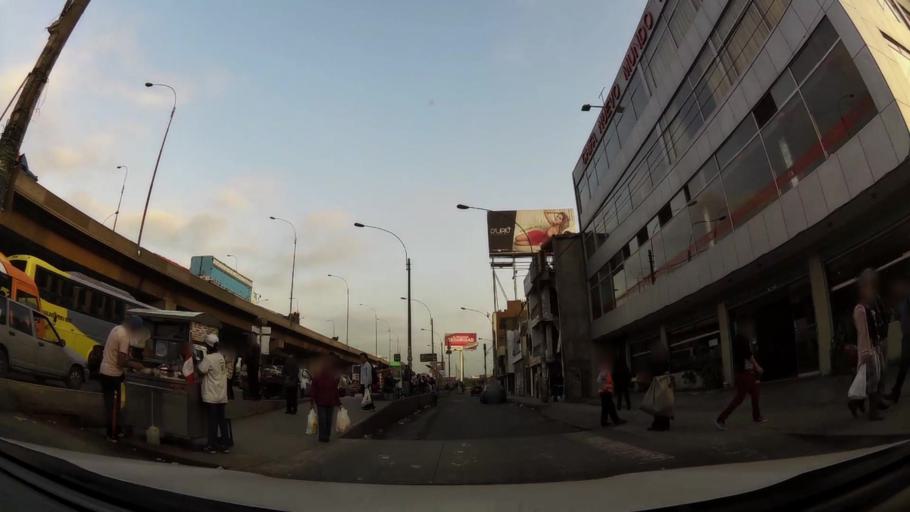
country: PE
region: Lima
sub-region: Lima
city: Independencia
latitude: -12.0064
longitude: -77.0621
